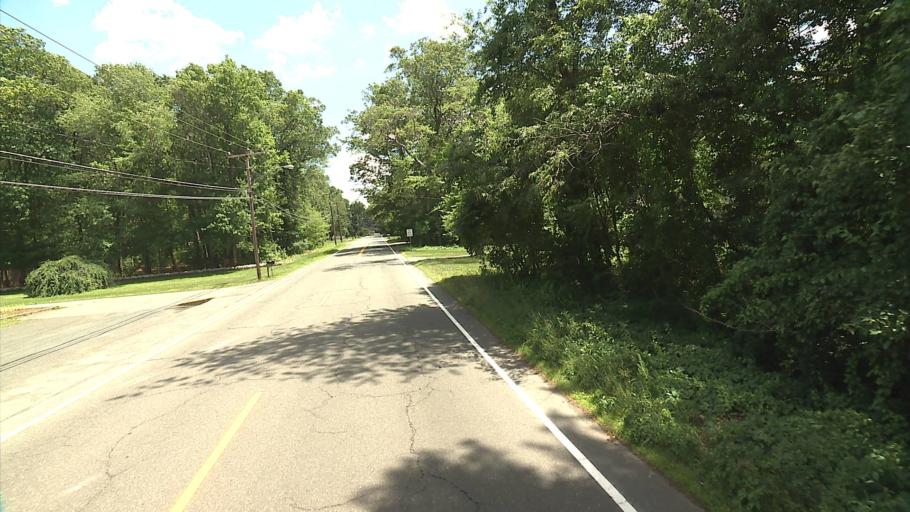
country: US
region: Connecticut
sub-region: Hartford County
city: Sherwood Manor
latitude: 42.0270
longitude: -72.5466
